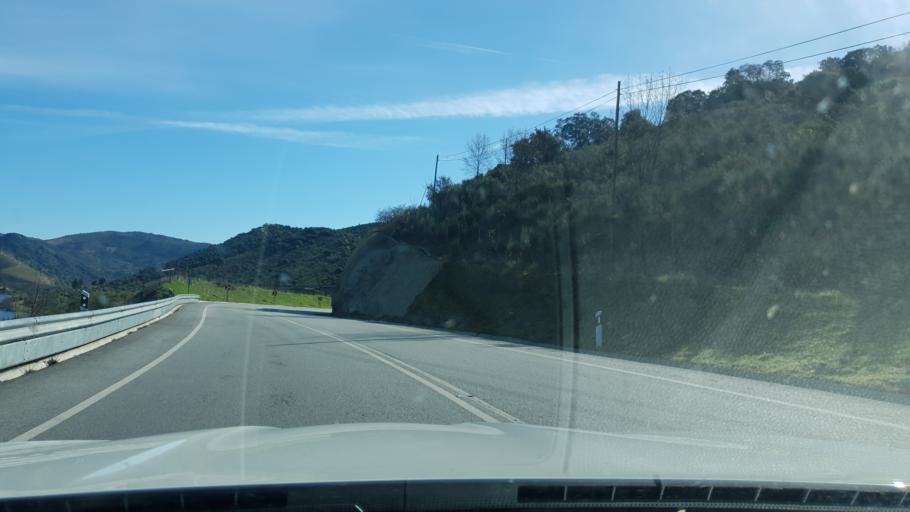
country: PT
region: Braganca
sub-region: Torre de Moncorvo
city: Torre de Moncorvo
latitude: 41.2120
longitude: -7.0875
